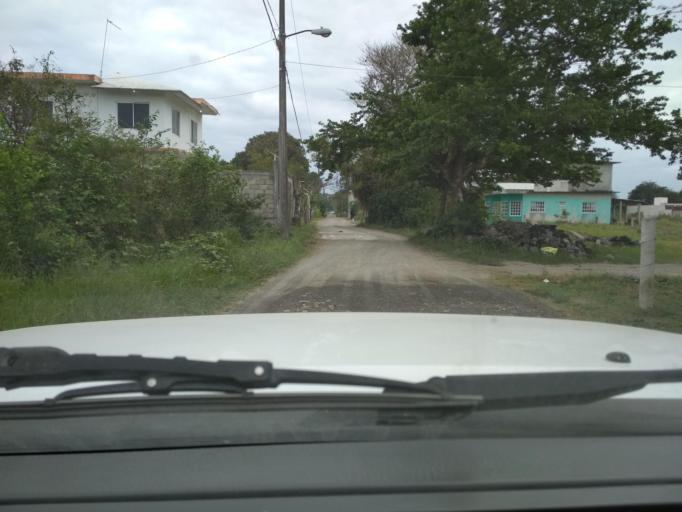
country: MX
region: Veracruz
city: El Tejar
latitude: 19.0733
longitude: -96.1427
